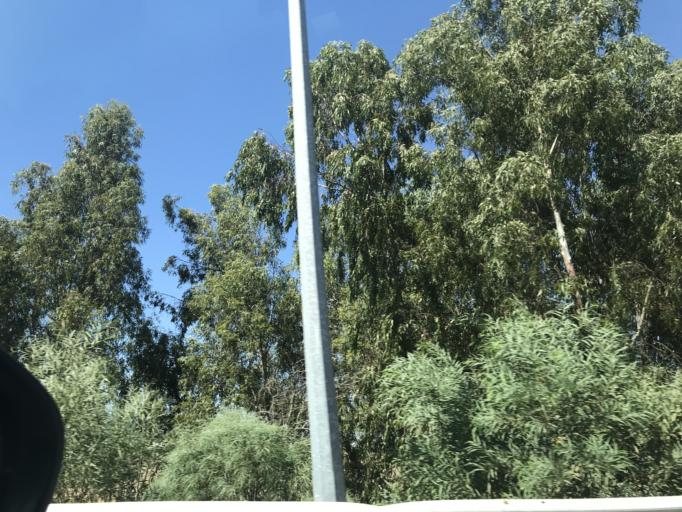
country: TR
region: Aydin
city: Aydin
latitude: 37.8184
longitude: 27.8439
